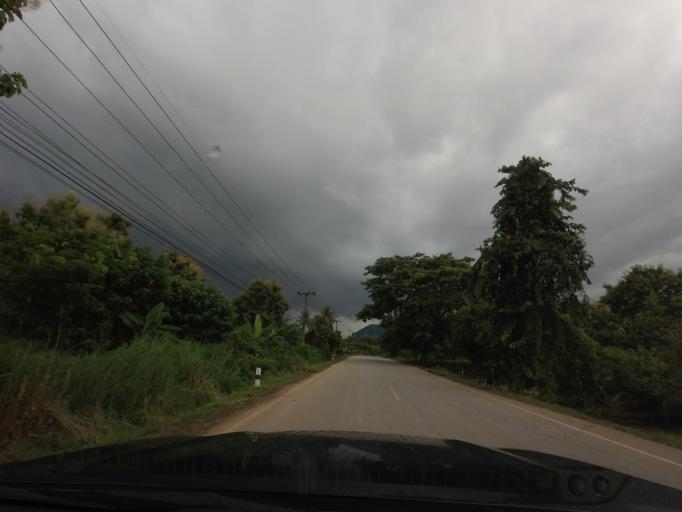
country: LA
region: Vientiane
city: Muang Sanakham
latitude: 17.9587
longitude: 101.7430
